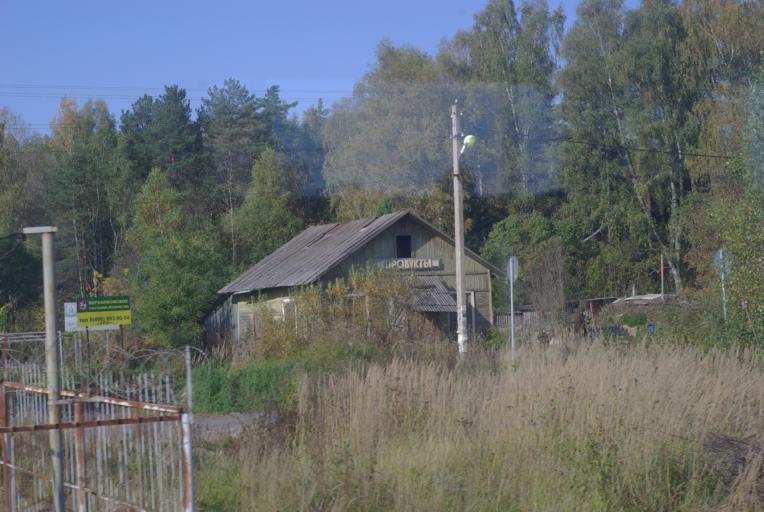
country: RU
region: Moskovskaya
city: Novo-Nikol'skoye
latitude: 56.5397
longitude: 37.5599
